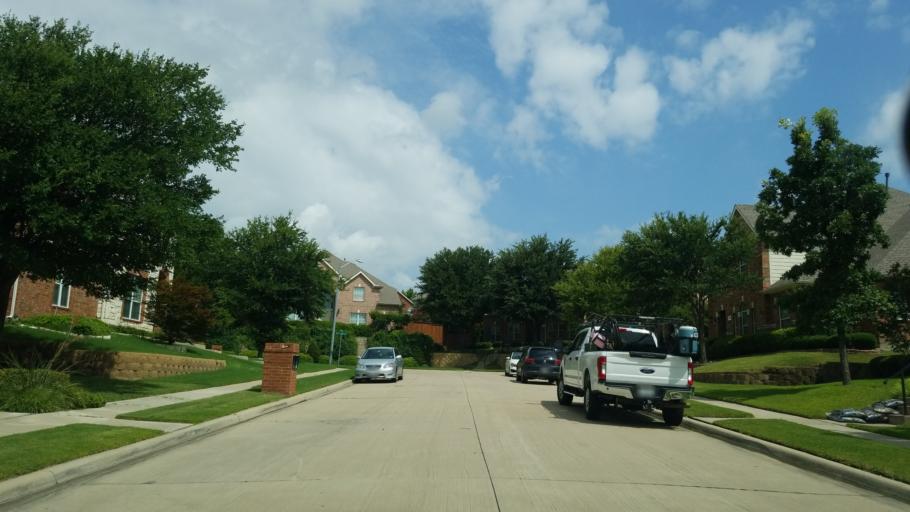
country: US
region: Texas
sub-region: Dallas County
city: Coppell
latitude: 32.9286
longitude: -96.9632
